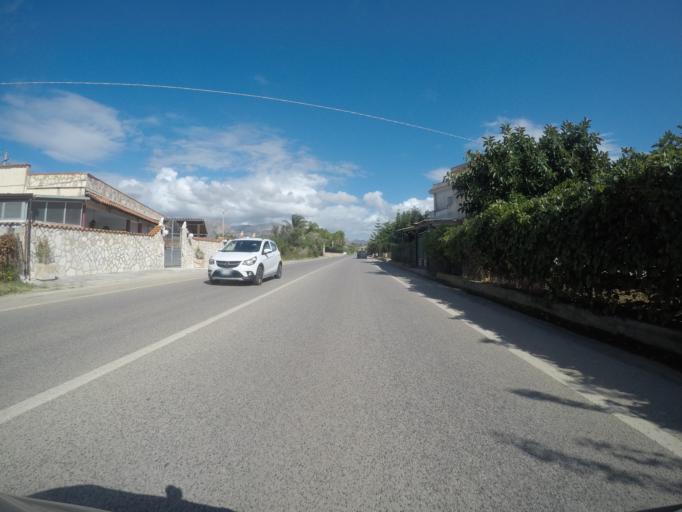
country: IT
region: Sicily
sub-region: Palermo
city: Trappeto
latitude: 38.0717
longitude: 13.0594
